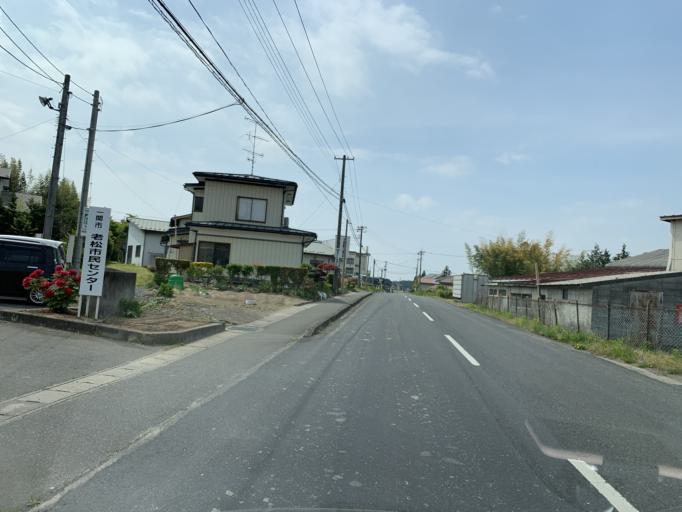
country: JP
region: Iwate
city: Ichinoseki
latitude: 38.8286
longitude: 141.2022
